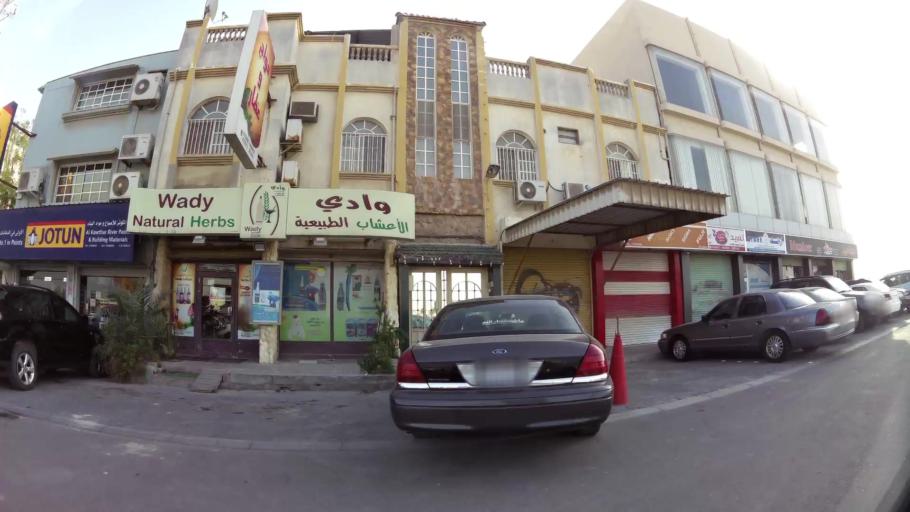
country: BH
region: Manama
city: Jidd Hafs
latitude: 26.2175
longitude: 50.5171
